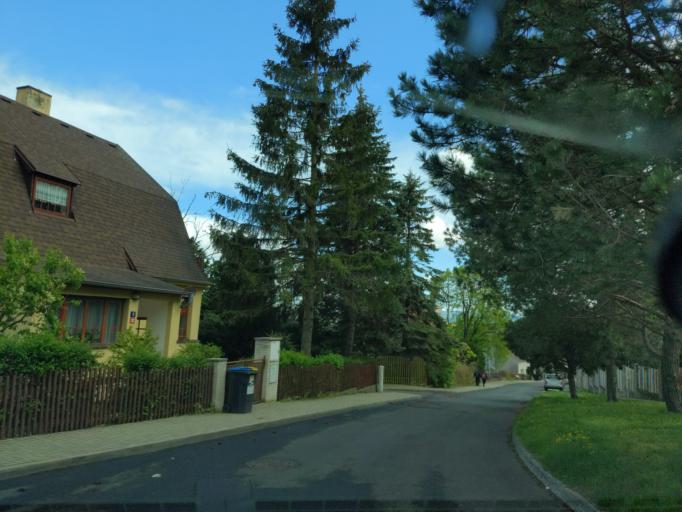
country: CZ
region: Ustecky
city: Krupka
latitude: 50.6848
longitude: 13.8743
